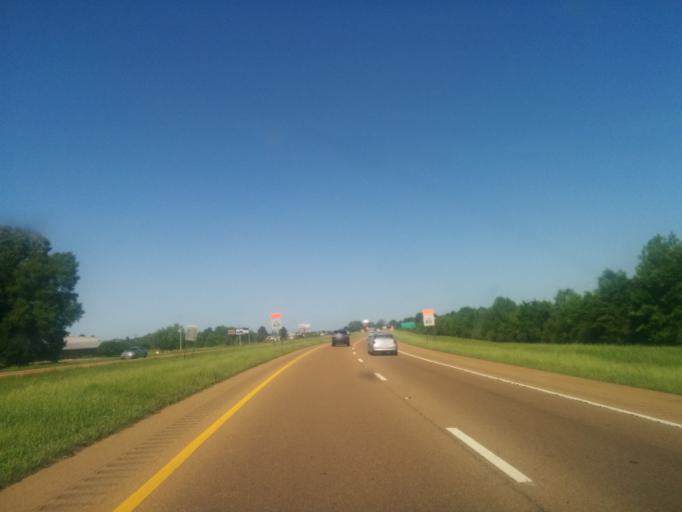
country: US
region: Mississippi
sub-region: Madison County
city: Madison
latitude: 32.5057
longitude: -90.1155
